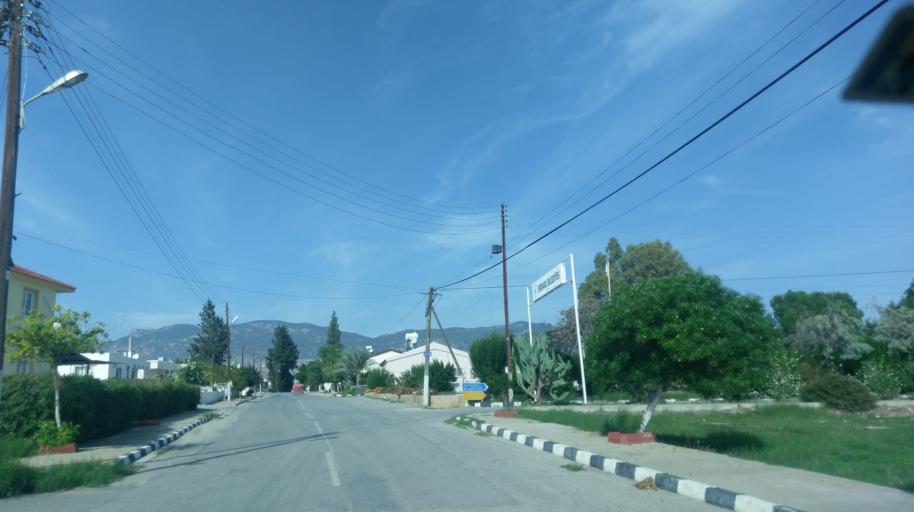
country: CY
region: Ammochostos
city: Lefkonoiko
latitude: 35.2507
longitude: 33.6049
